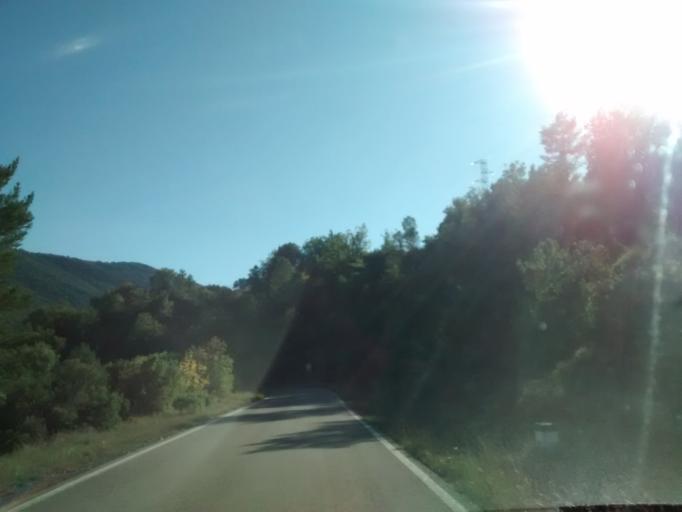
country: ES
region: Aragon
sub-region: Provincia de Huesca
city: Loarre
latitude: 42.4100
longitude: -0.6462
